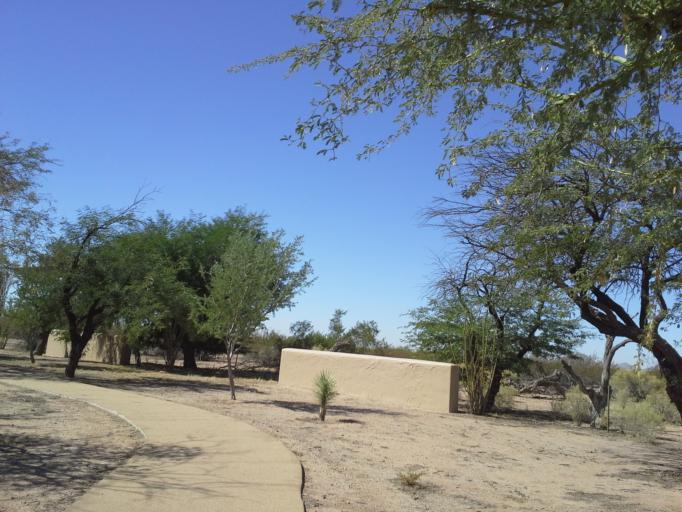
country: US
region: Arizona
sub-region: Pinal County
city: Coolidge
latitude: 32.9958
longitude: -111.5368
